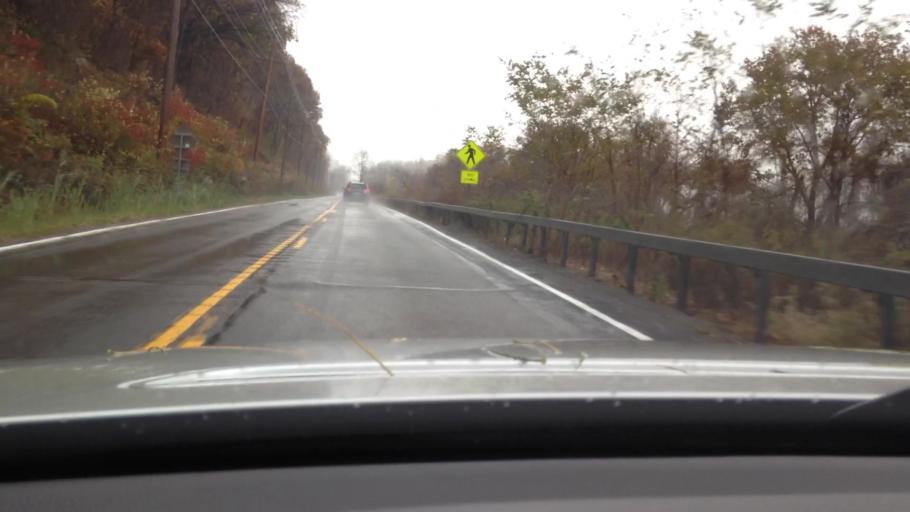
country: US
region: New York
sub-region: Putnam County
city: Cold Spring
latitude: 41.4350
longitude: -73.9711
